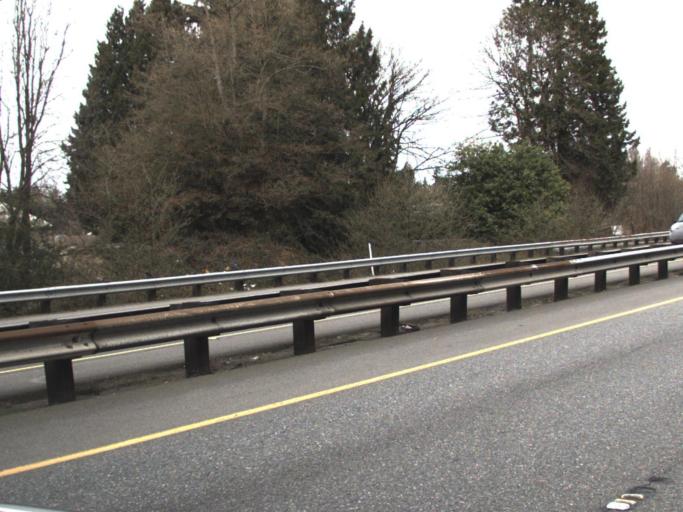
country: US
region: Washington
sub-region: King County
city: Boulevard Park
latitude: 47.4834
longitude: -122.3272
